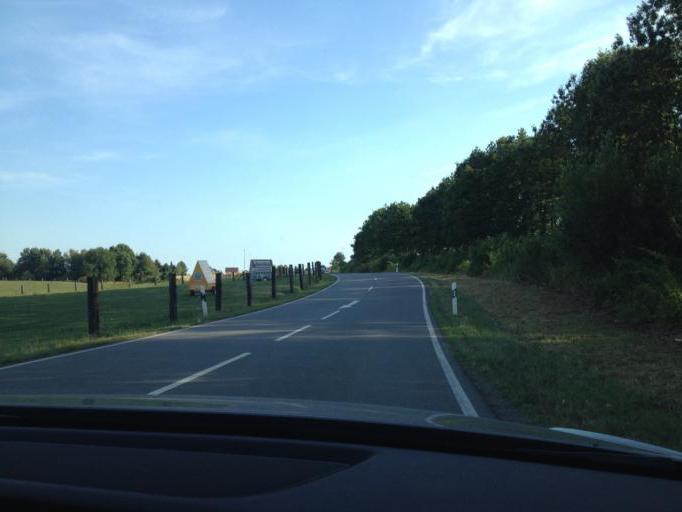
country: DE
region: Saarland
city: Oberthal
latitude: 49.5558
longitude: 7.0619
